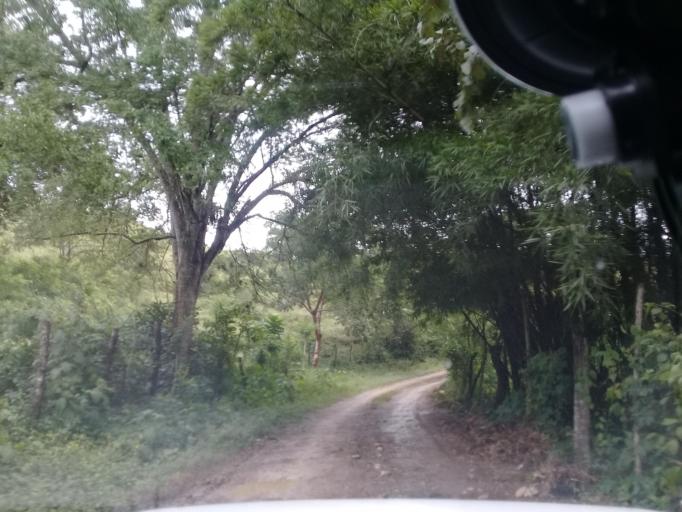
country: MX
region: Veracruz
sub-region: Chalma
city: San Pedro Coyutla
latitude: 21.2378
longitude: -98.4301
